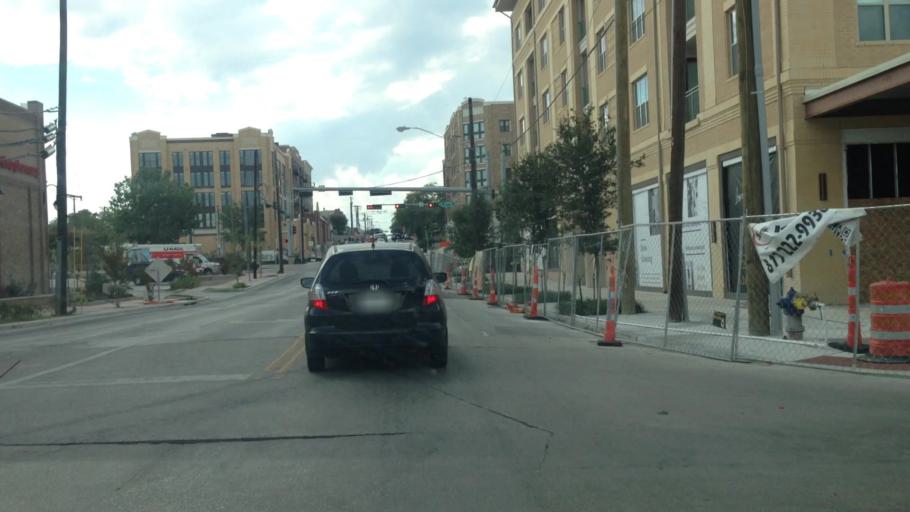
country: US
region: Texas
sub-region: Dallas County
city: Dallas
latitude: 32.7495
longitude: -96.8229
